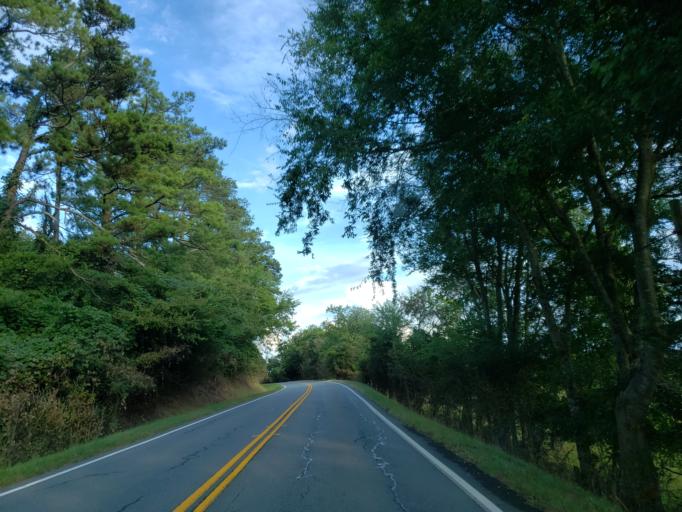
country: US
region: Georgia
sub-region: Bartow County
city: Euharlee
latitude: 34.2418
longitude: -84.8878
